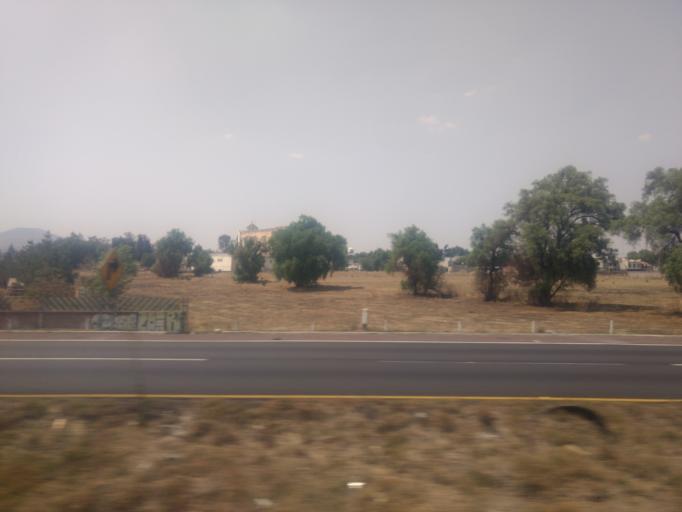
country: MX
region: Mexico
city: Acolman
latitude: 19.6296
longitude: -98.9146
